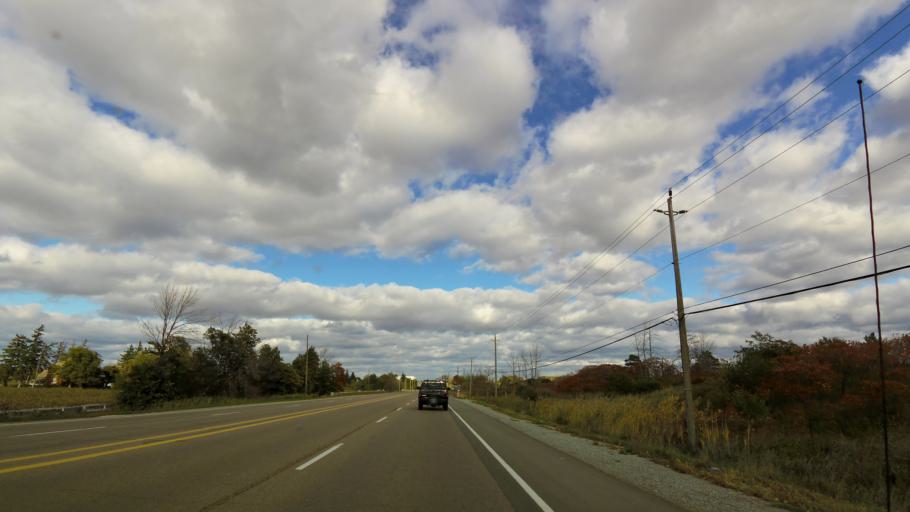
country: CA
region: Ontario
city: Burlington
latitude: 43.4244
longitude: -79.7884
